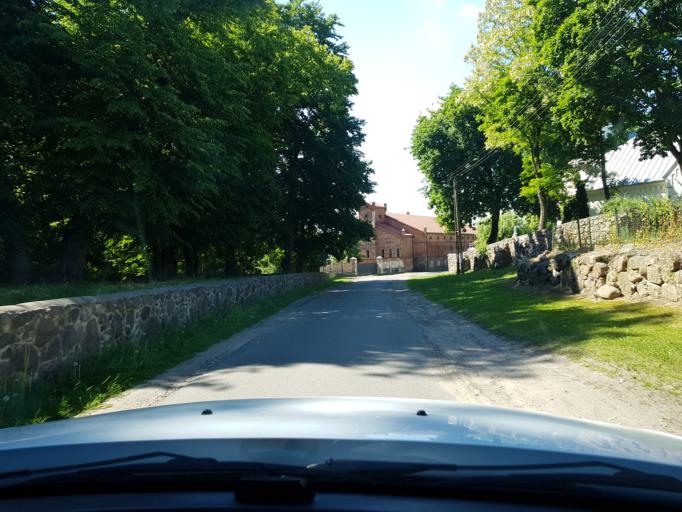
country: PL
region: West Pomeranian Voivodeship
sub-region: Powiat gryfinski
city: Banie
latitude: 53.1368
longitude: 14.5479
